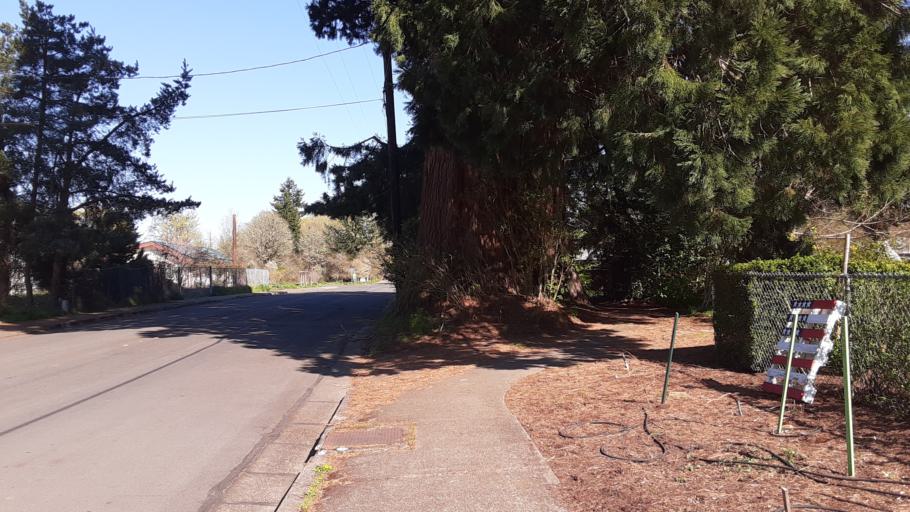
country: US
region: Oregon
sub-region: Benton County
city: Corvallis
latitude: 44.5452
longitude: -123.2571
